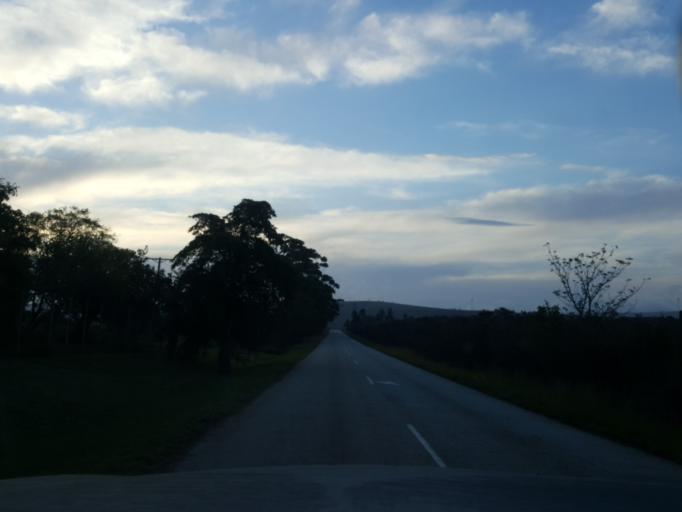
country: ZA
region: Eastern Cape
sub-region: Cacadu District Municipality
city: Grahamstown
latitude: -33.3871
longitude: 26.4727
